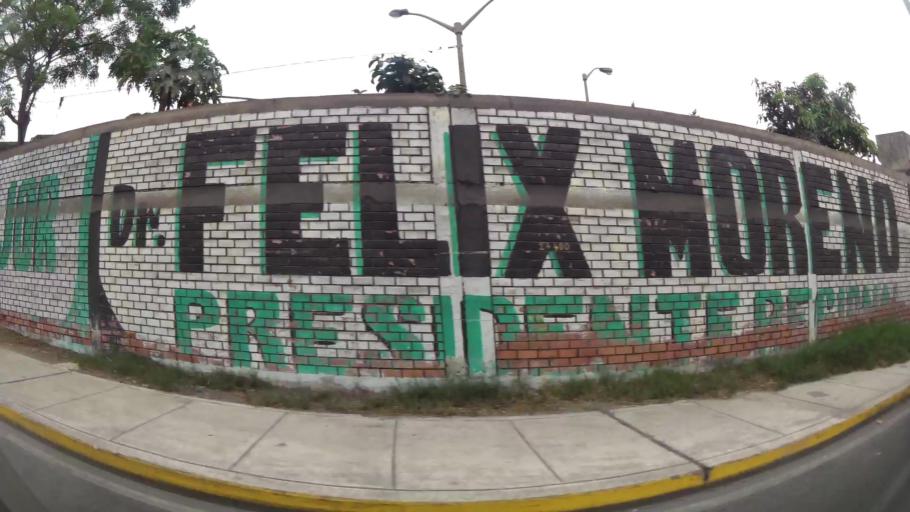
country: PE
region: Callao
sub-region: Callao
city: Callao
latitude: -12.0491
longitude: -77.1386
